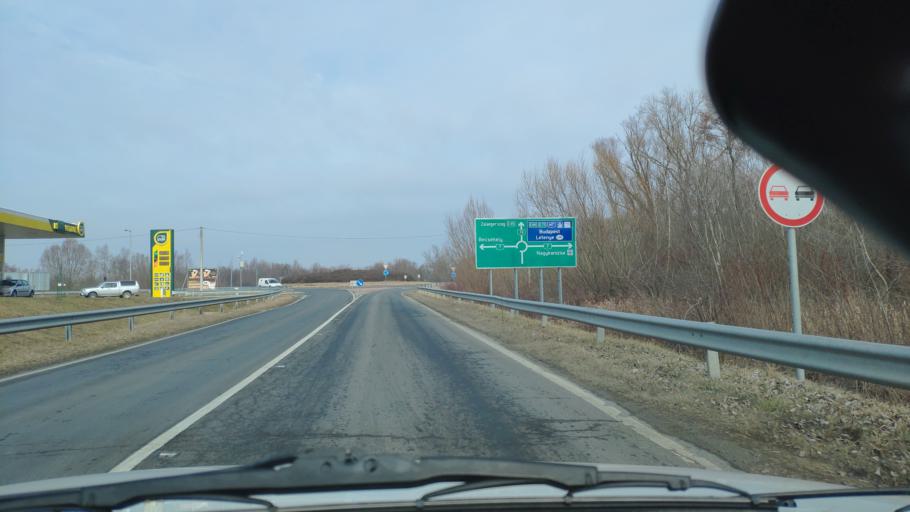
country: HU
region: Zala
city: Nagykanizsa
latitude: 46.4658
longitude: 16.9690
